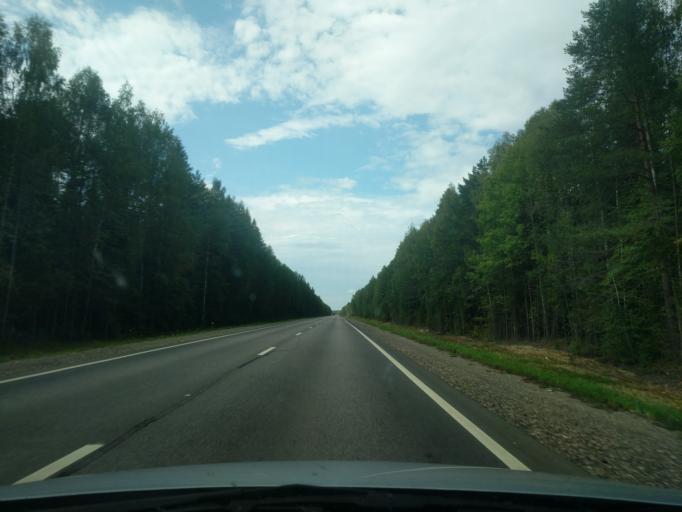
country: RU
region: Kostroma
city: Kadyy
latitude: 57.7965
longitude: 42.9127
